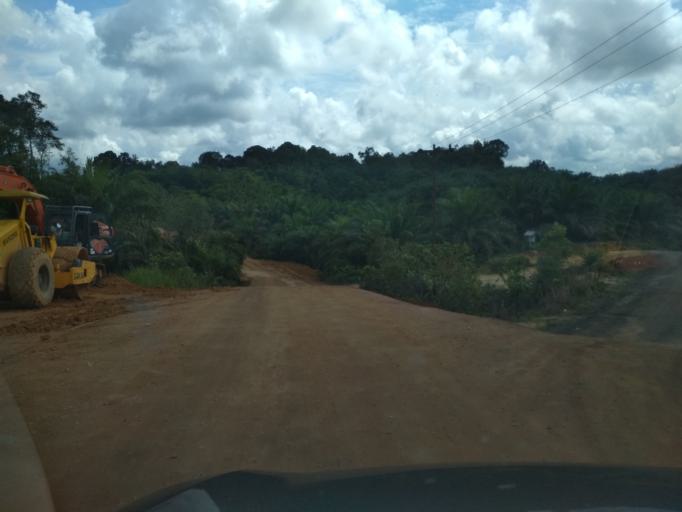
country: ID
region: West Kalimantan
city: Tayan
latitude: 0.5356
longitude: 110.0878
